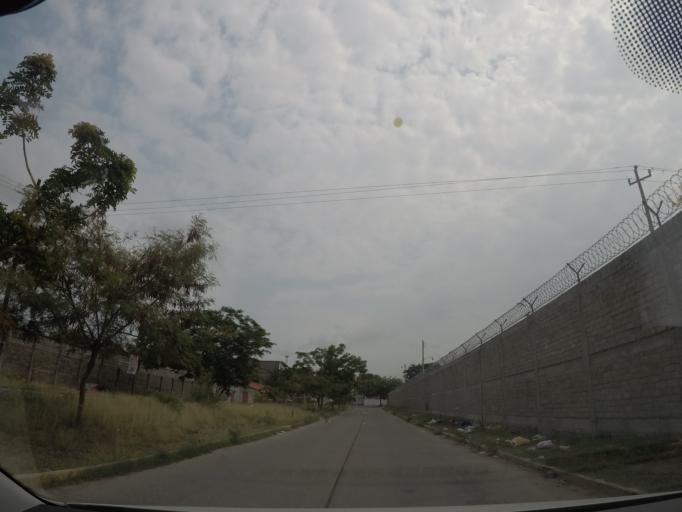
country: MX
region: Oaxaca
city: Juchitan de Zaragoza
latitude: 16.4456
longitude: -95.0214
